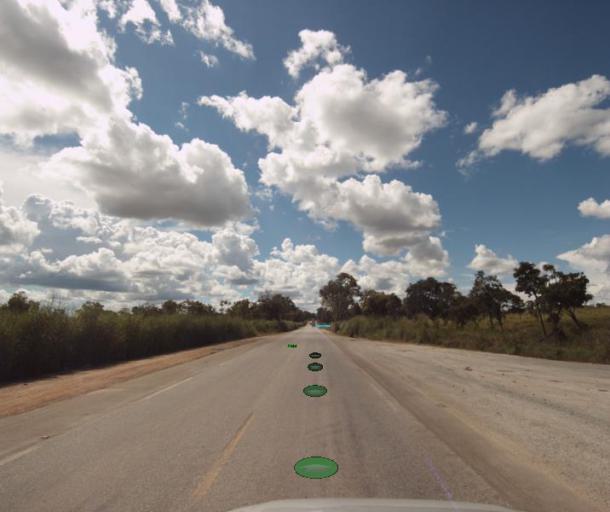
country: BR
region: Goias
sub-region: Porangatu
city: Porangatu
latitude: -13.6327
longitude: -49.0419
